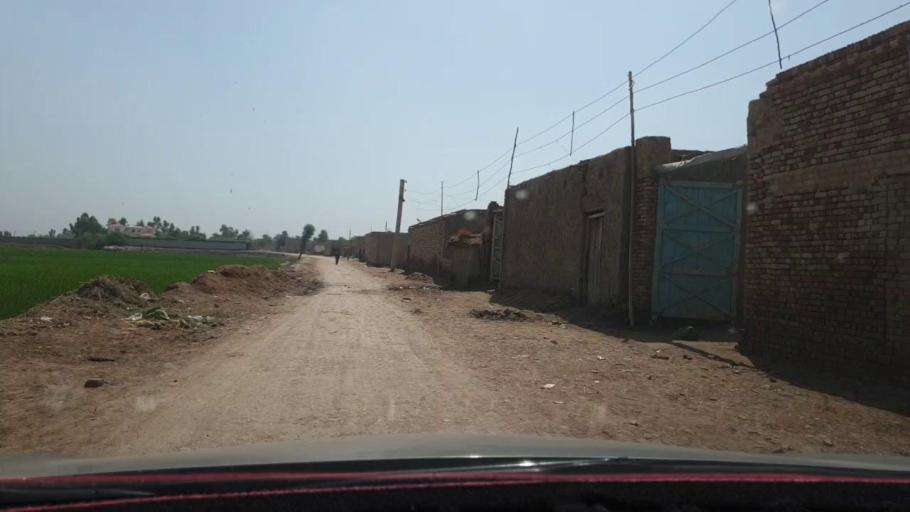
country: PK
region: Sindh
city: Warah
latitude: 27.4850
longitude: 67.8241
